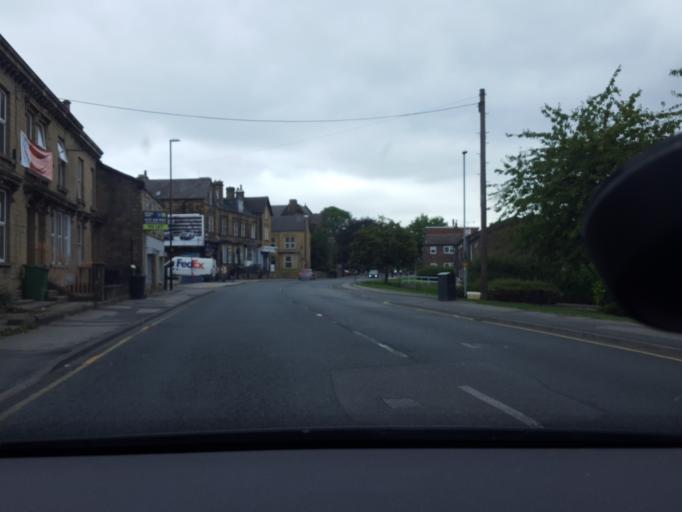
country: GB
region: England
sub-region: City and Borough of Leeds
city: Horsforth
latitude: 53.8132
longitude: -1.6306
